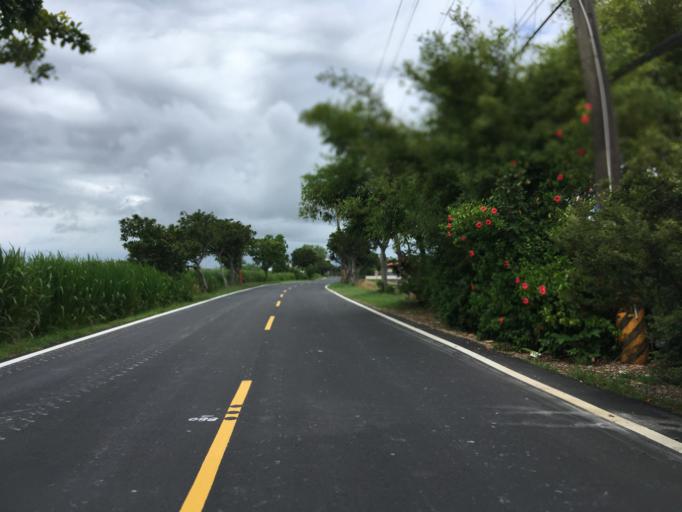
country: TW
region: Taiwan
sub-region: Yilan
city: Yilan
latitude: 24.6846
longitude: 121.8084
